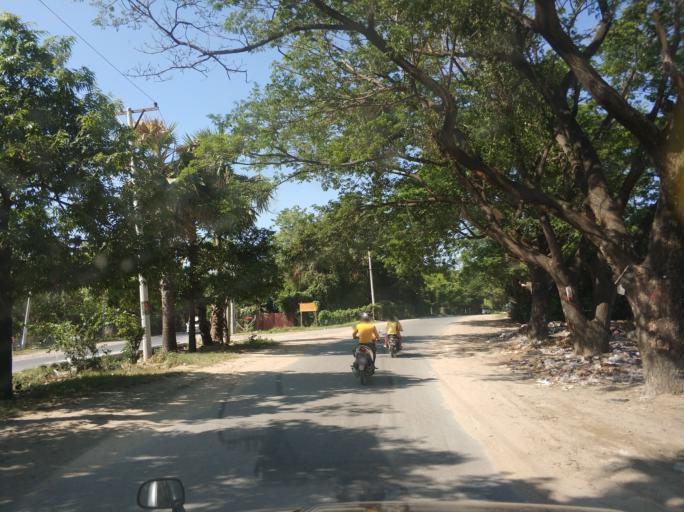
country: MM
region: Mandalay
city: Mandalay
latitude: 21.9559
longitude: 96.0521
